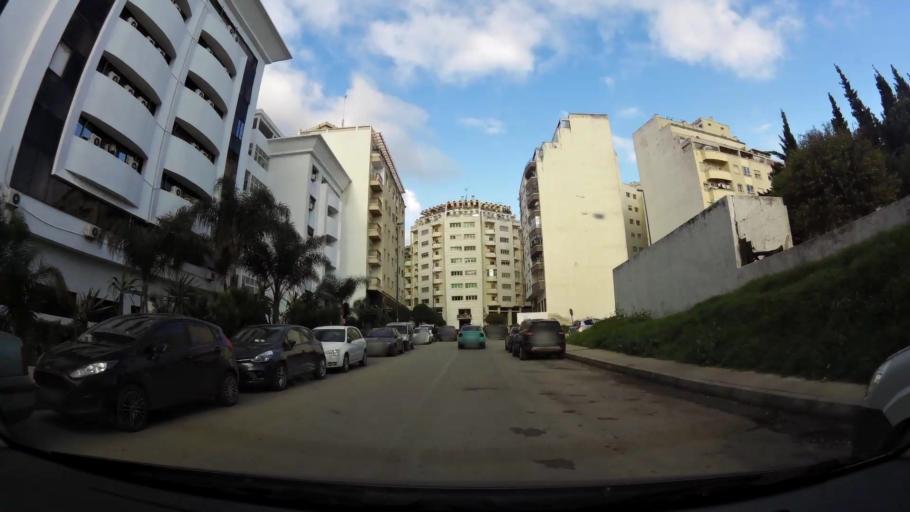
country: MA
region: Tanger-Tetouan
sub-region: Tanger-Assilah
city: Tangier
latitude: 35.7721
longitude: -5.8038
